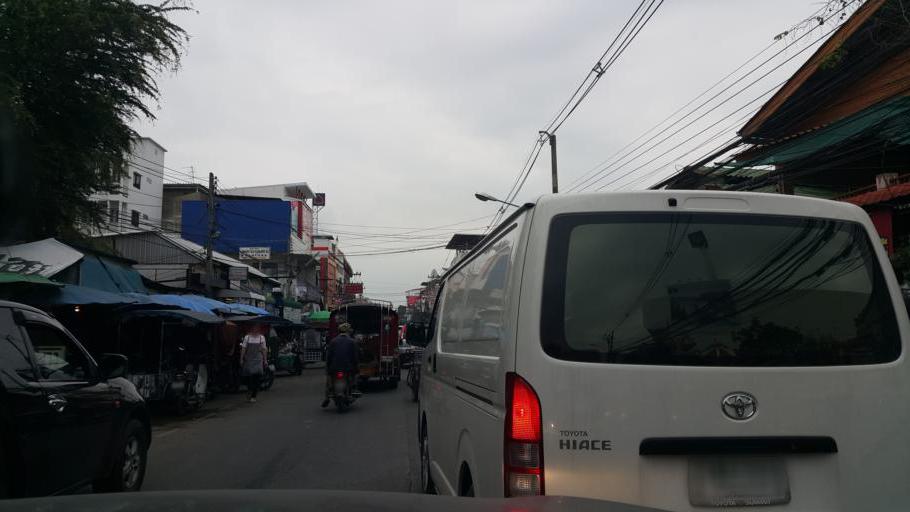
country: TH
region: Chiang Mai
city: Chiang Mai
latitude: 18.7964
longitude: 98.9967
